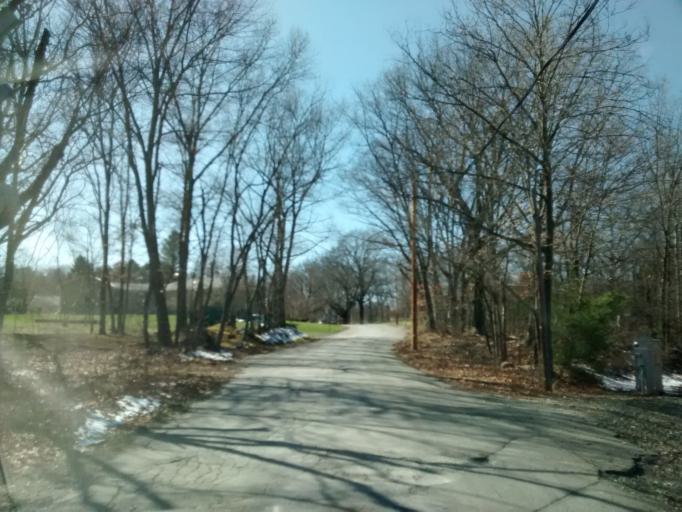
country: US
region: Massachusetts
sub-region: Worcester County
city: Millbury
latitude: 42.1871
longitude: -71.7469
